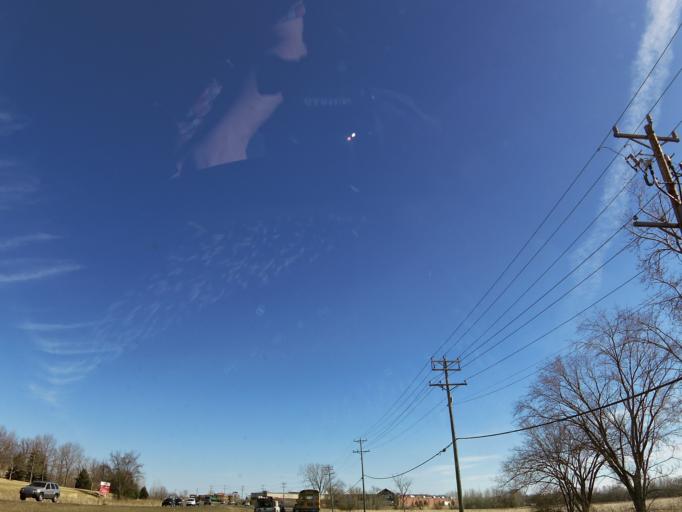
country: US
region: Minnesota
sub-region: Hennepin County
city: Plymouth
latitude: 45.0201
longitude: -93.4901
